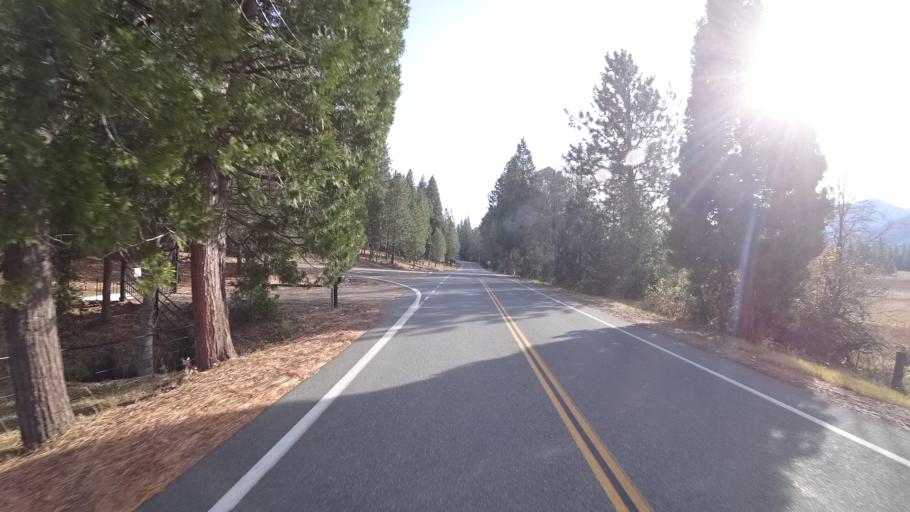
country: US
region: California
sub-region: Siskiyou County
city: Weed
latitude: 41.3999
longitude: -122.4207
